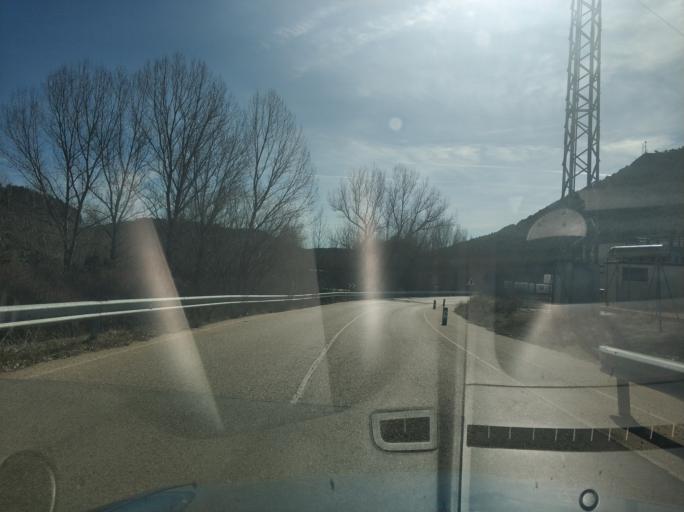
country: ES
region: Castille and Leon
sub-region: Provincia de Soria
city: San Leonardo de Yague
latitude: 41.8268
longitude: -3.0828
